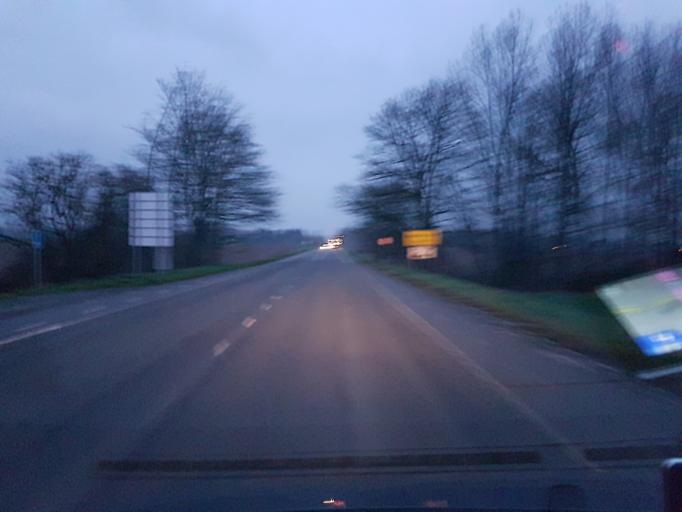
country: BE
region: Wallonia
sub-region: Province de Namur
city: Eghezee
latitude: 50.6019
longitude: 4.9012
